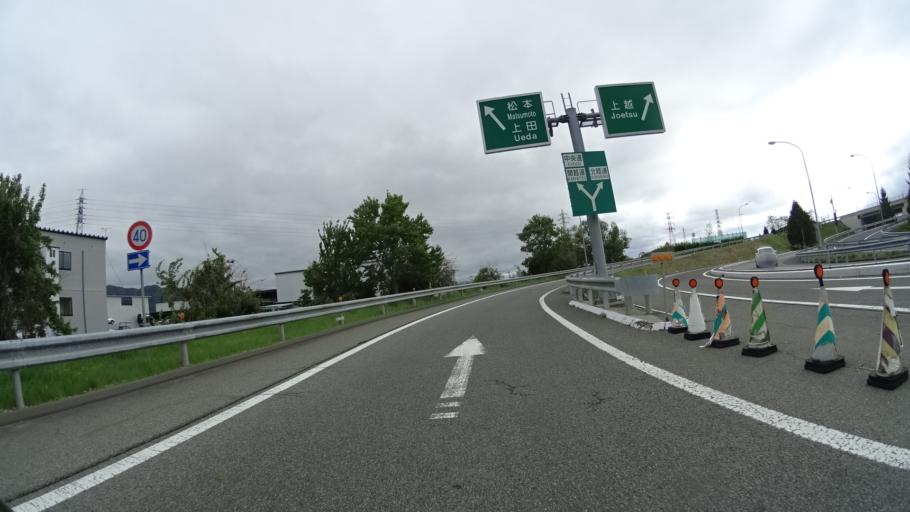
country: JP
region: Nagano
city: Nakano
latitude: 36.7303
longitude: 138.3190
